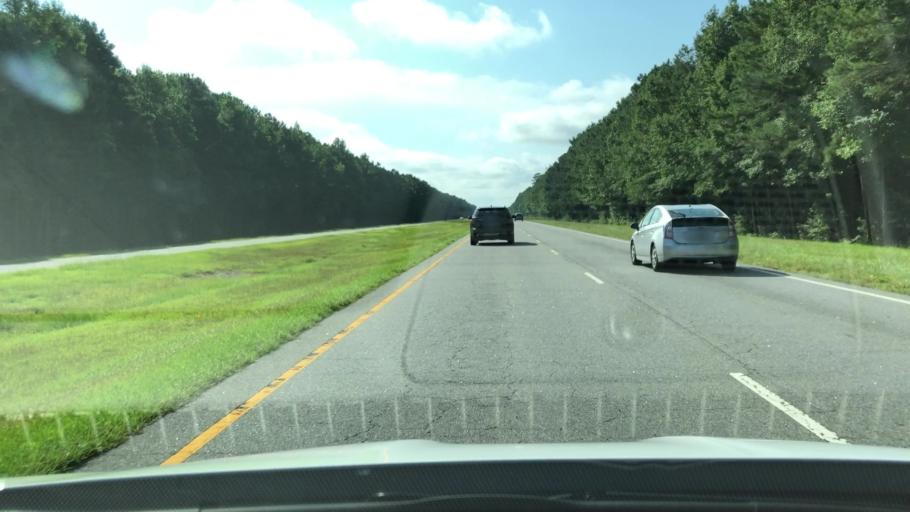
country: US
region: North Carolina
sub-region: Pasquotank County
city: Elizabeth City
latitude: 36.3941
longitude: -76.3256
